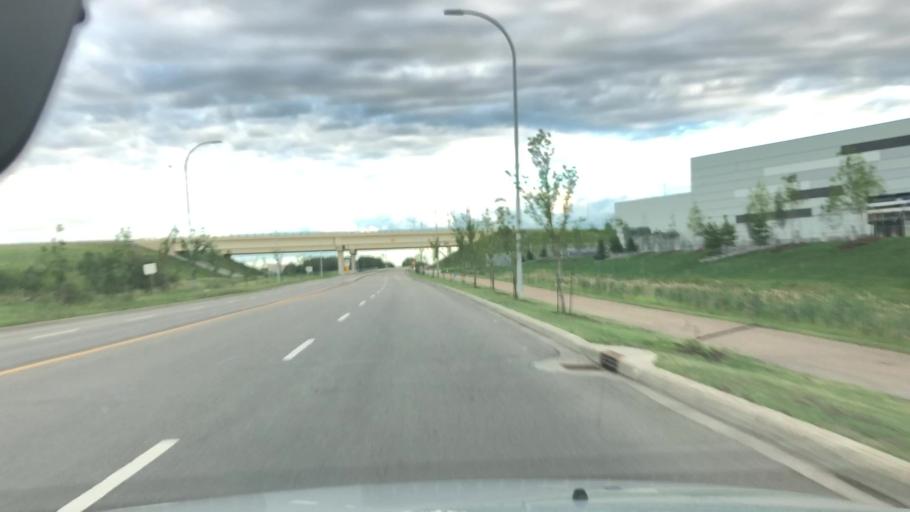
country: CA
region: Alberta
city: St. Albert
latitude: 53.6354
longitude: -113.5660
